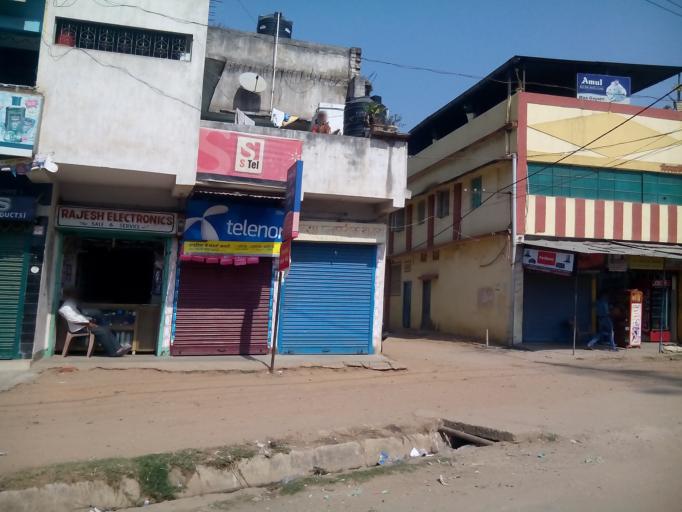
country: IN
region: Jharkhand
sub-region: Ranchi
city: Ranchi
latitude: 23.3765
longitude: 85.3543
